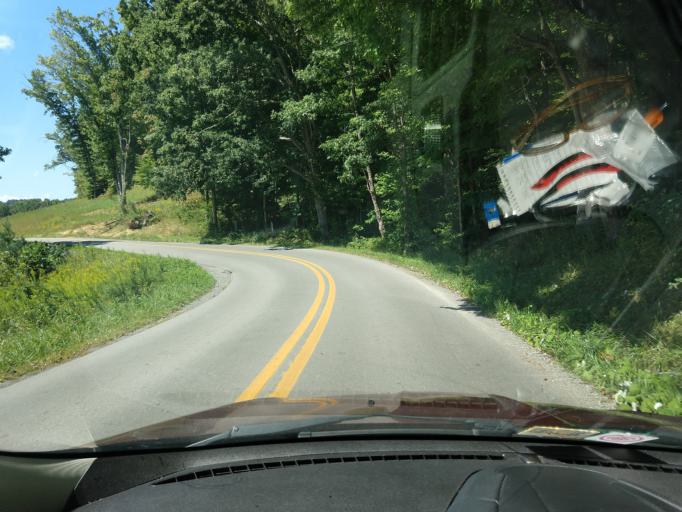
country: US
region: West Virginia
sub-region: Nicholas County
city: Summersville
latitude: 38.2766
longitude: -80.7678
